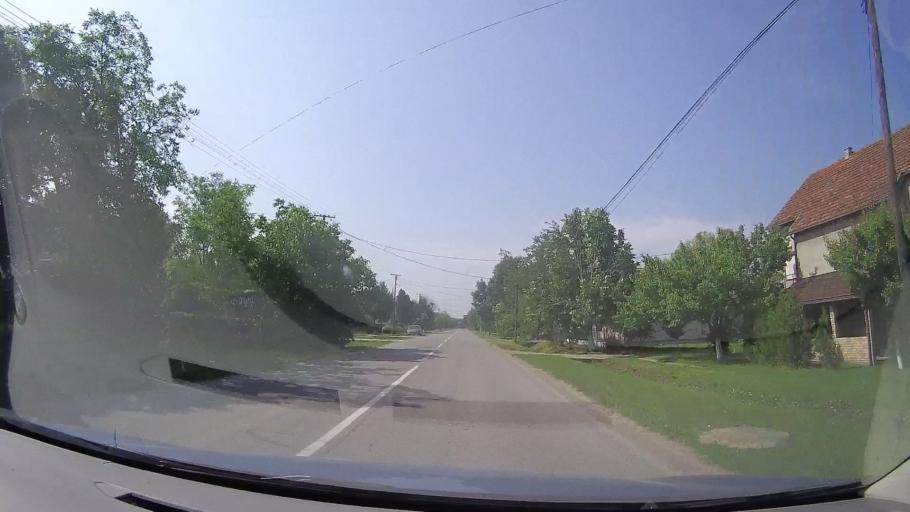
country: RS
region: Autonomna Pokrajina Vojvodina
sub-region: Srednjebanatski Okrug
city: Secanj
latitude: 45.3718
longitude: 20.7776
